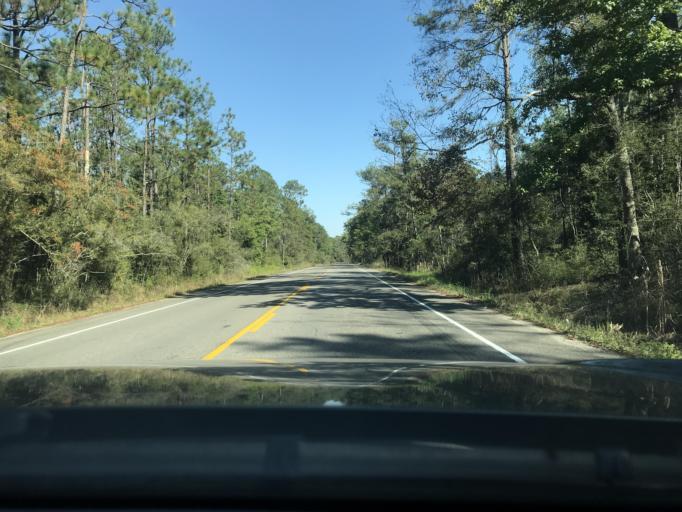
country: US
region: Louisiana
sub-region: Calcasieu Parish
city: Westlake
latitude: 30.3053
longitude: -93.2569
